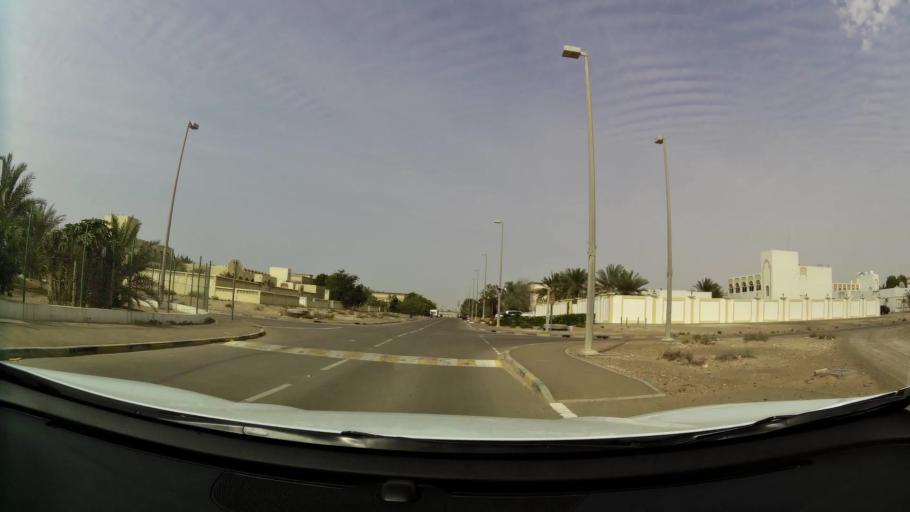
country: AE
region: Abu Dhabi
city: Abu Dhabi
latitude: 24.5574
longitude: 54.6883
